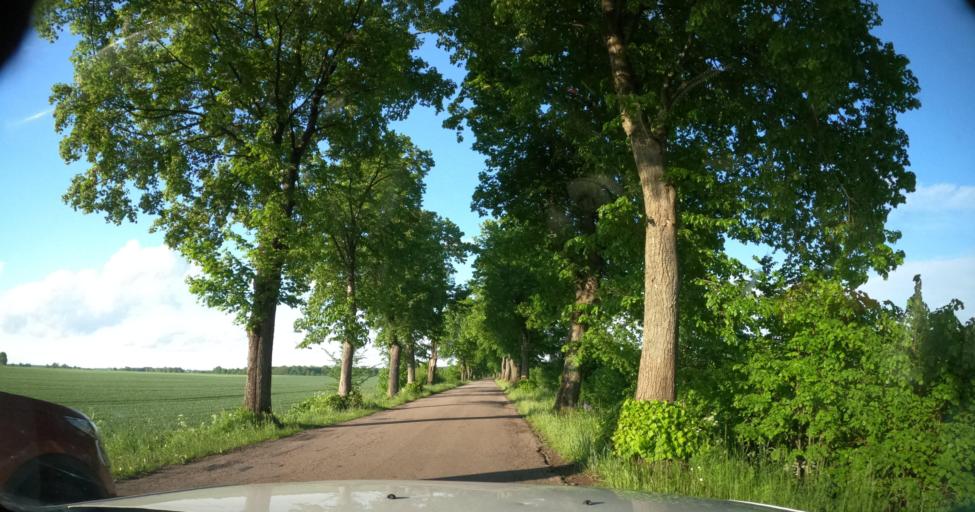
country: PL
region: Warmian-Masurian Voivodeship
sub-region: Powiat braniewski
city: Braniewo
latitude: 54.2745
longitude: 19.8374
